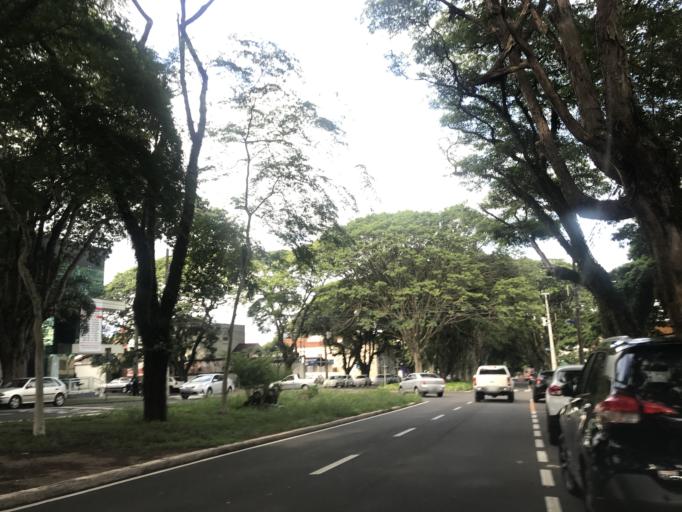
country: BR
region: Parana
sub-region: Maringa
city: Maringa
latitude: -23.4283
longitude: -51.9574
